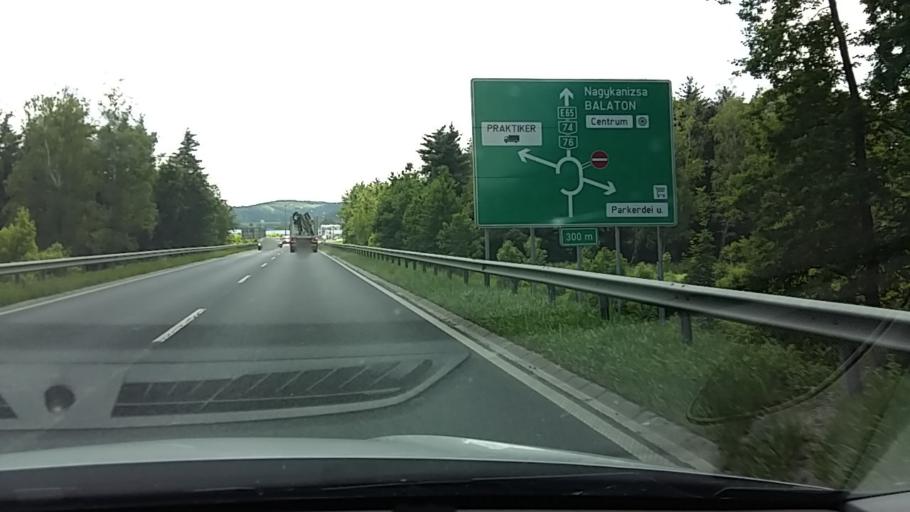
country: HU
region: Zala
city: Zalaegerszeg
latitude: 46.8485
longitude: 16.8637
